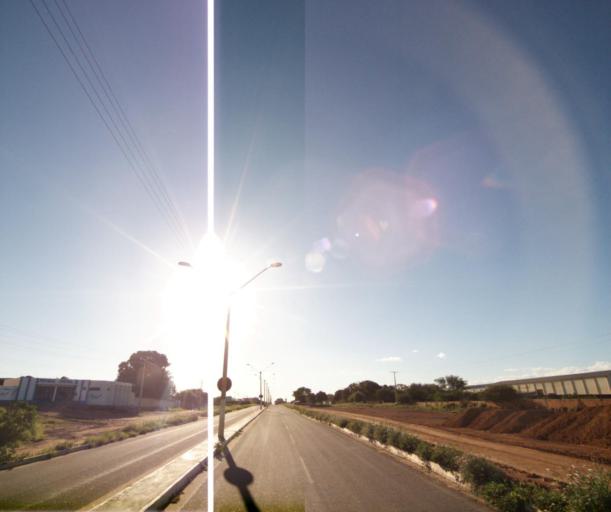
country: BR
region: Bahia
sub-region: Guanambi
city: Guanambi
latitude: -14.2100
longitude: -42.7816
